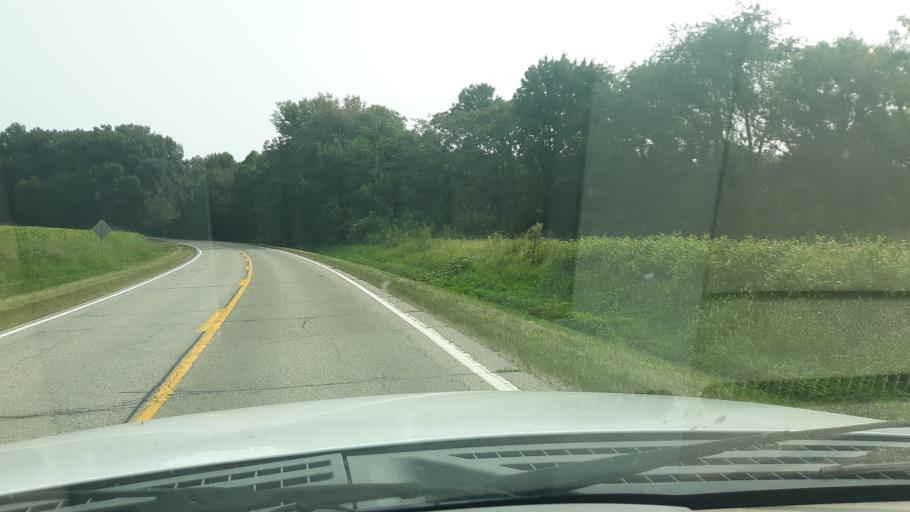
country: US
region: Illinois
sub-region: Edwards County
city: Grayville
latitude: 38.3137
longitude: -87.9337
